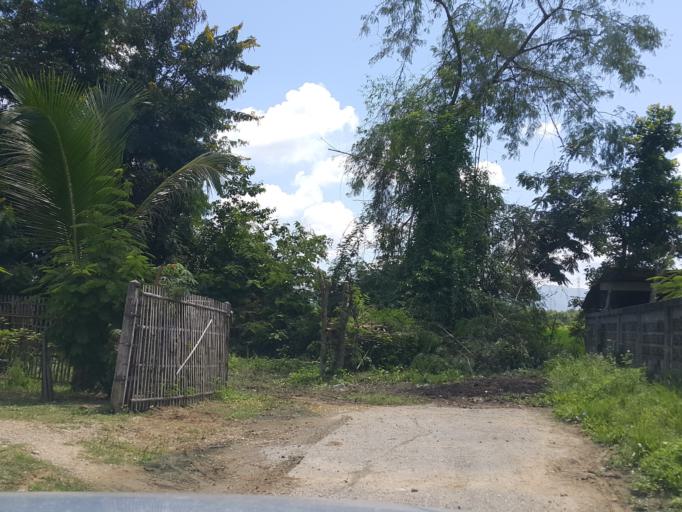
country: TH
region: Chiang Mai
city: San Kamphaeng
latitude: 18.6991
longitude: 99.1066
